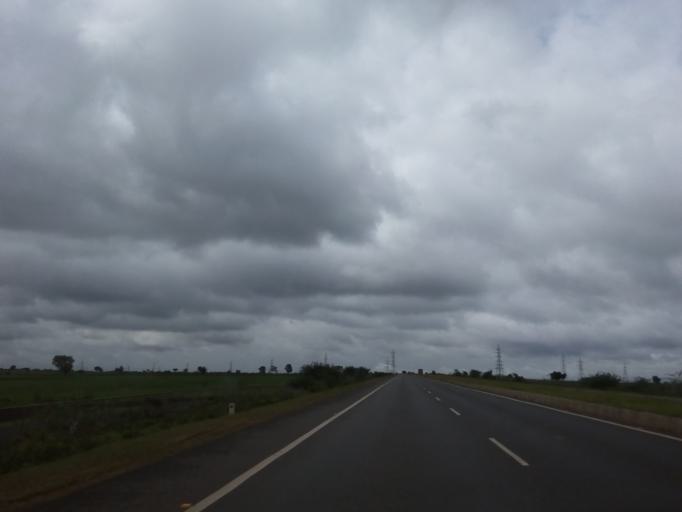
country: IN
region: Karnataka
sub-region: Haveri
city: Haveri
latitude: 14.8190
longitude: 75.3704
